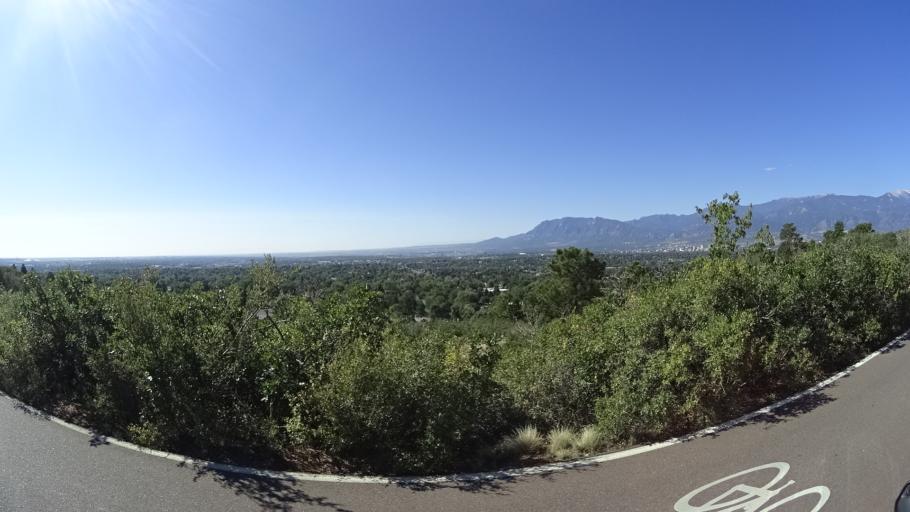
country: US
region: Colorado
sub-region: El Paso County
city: Colorado Springs
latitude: 38.8719
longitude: -104.7725
